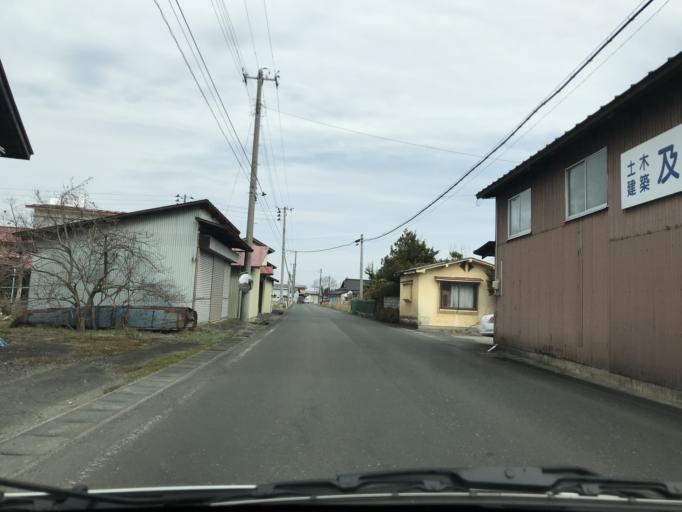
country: JP
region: Iwate
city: Mizusawa
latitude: 39.1568
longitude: 141.0976
